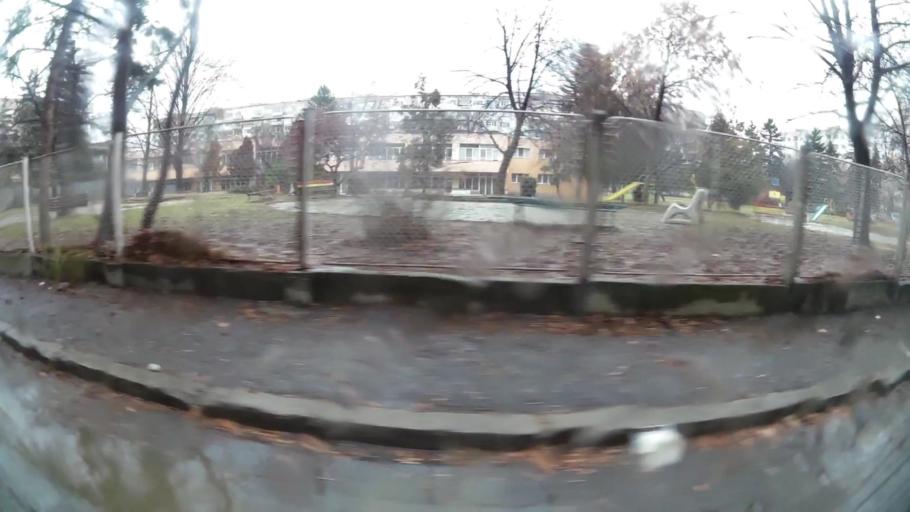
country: BG
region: Sofia-Capital
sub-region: Stolichna Obshtina
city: Sofia
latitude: 42.6606
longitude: 23.3632
